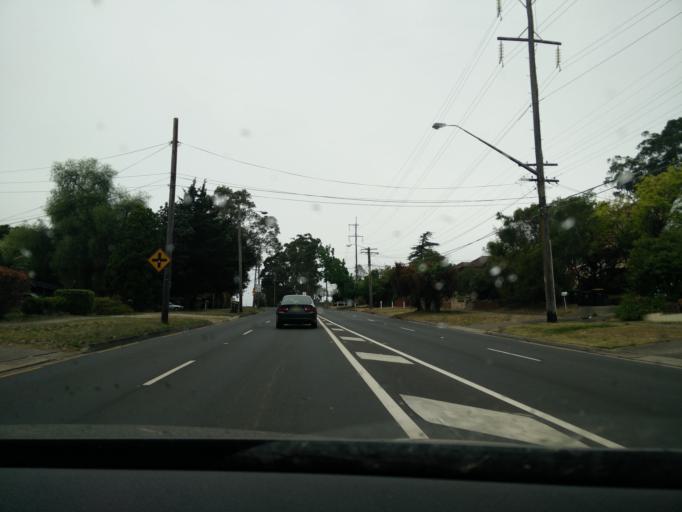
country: AU
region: New South Wales
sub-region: Parramatta
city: Carlingford
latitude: -33.7765
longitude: 151.0577
